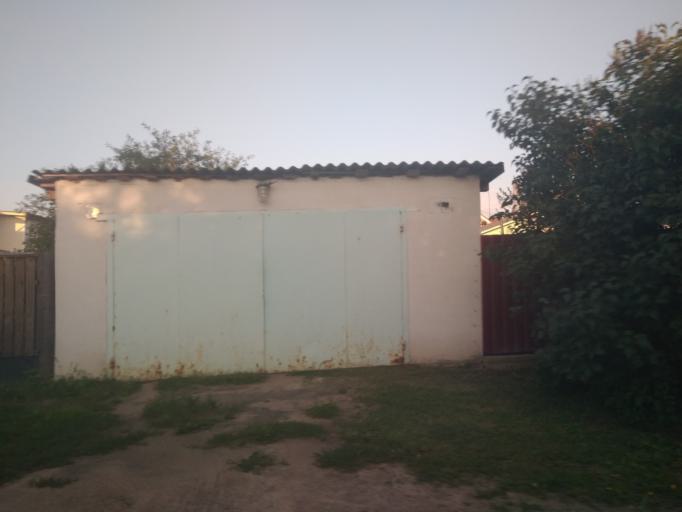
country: BY
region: Minsk
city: Minsk
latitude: 53.9387
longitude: 27.5592
